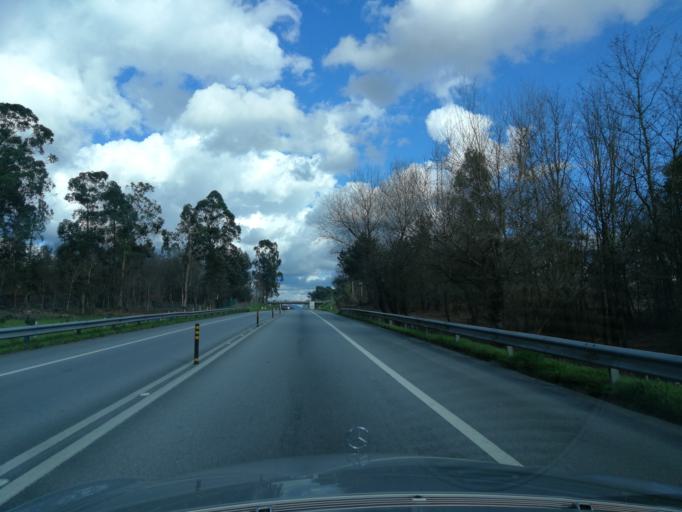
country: PT
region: Braga
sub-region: Vila Verde
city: Vila Verde
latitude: 41.6169
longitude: -8.4432
